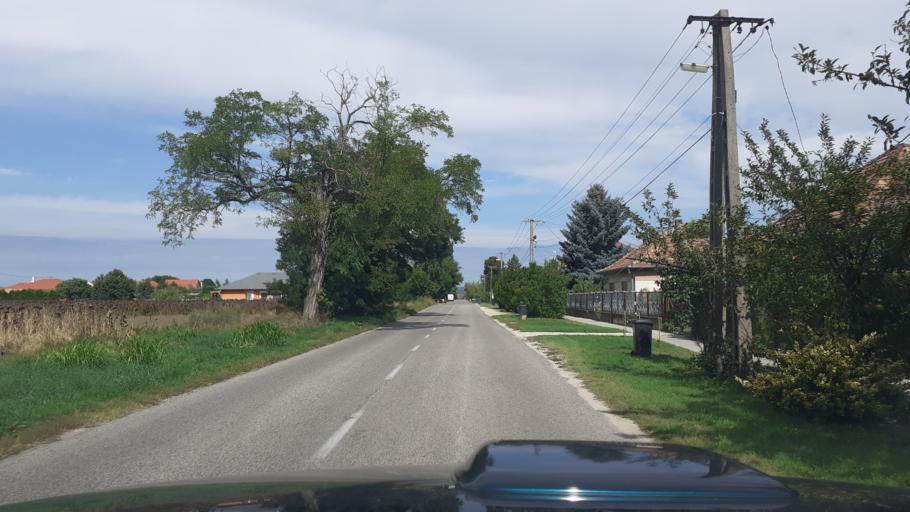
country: HU
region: Fejer
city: Seregelyes
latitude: 47.1687
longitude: 18.5710
